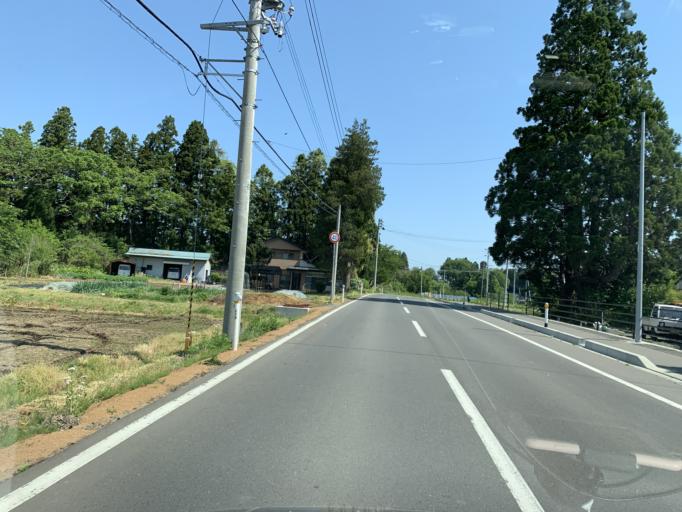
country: JP
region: Iwate
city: Mizusawa
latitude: 39.0887
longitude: 141.0693
